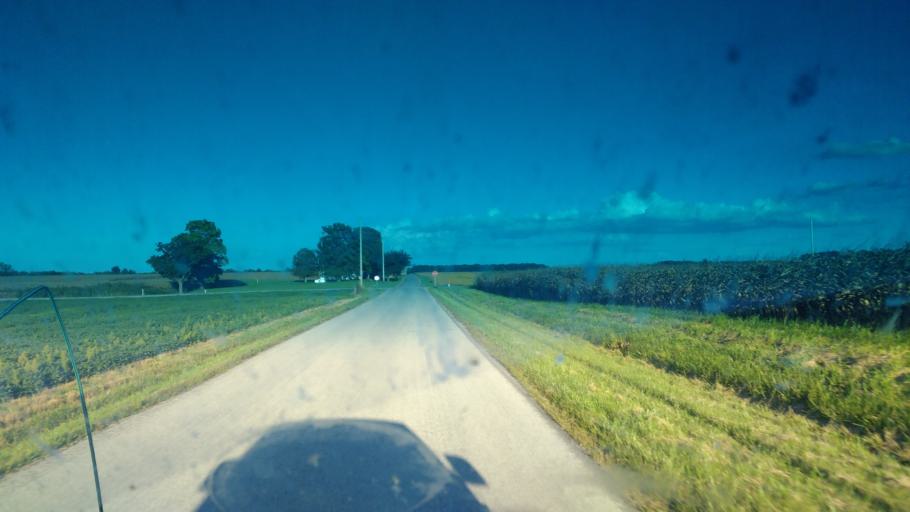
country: US
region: Ohio
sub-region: Wyandot County
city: Upper Sandusky
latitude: 40.8909
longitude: -83.2778
